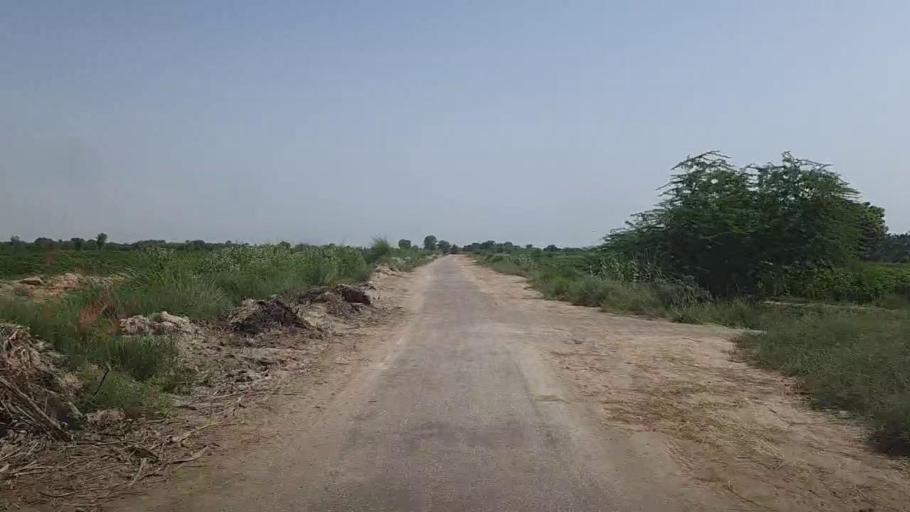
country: PK
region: Sindh
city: Pad Idan
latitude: 26.8332
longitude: 68.3306
